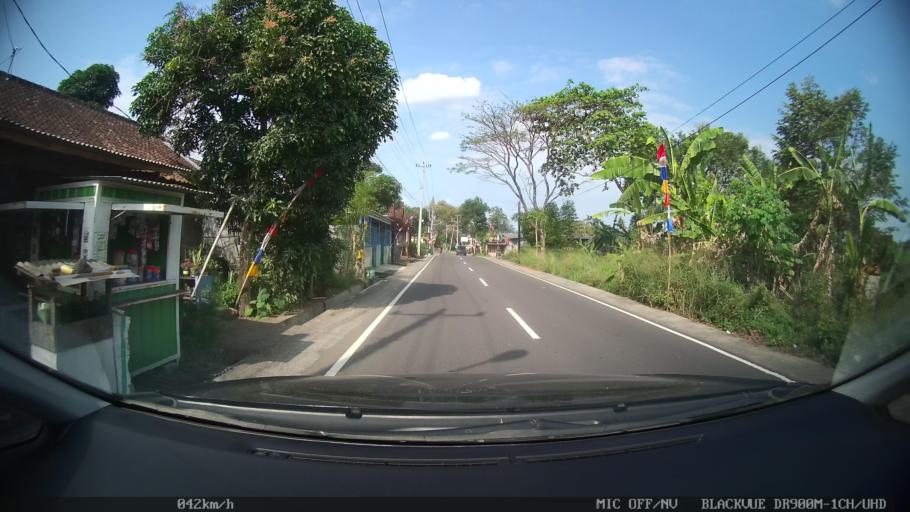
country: ID
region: Daerah Istimewa Yogyakarta
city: Depok
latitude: -7.7277
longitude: 110.4263
